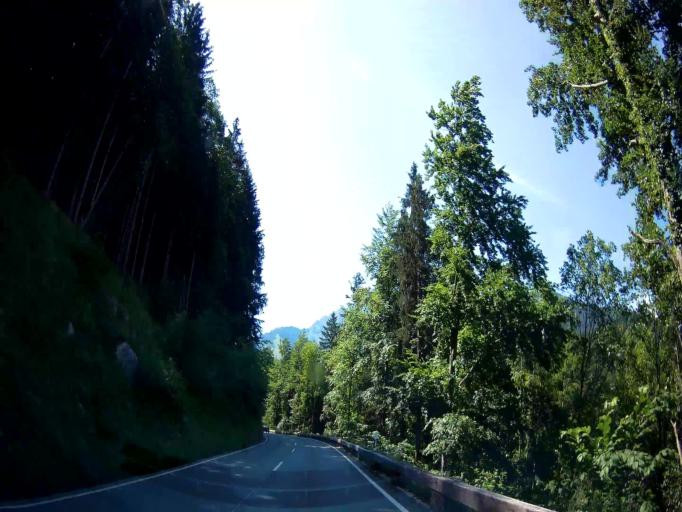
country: DE
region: Bavaria
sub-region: Upper Bavaria
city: Berchtesgaden
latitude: 47.6369
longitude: 13.0543
